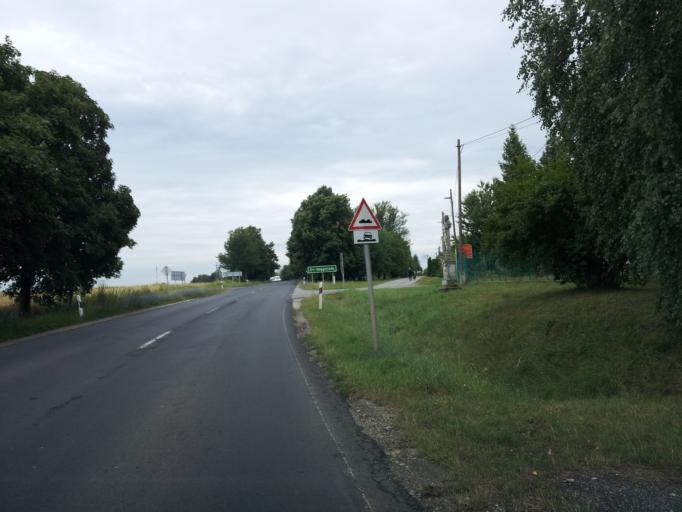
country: HU
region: Vas
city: Kormend
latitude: 46.9735
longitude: 16.6341
